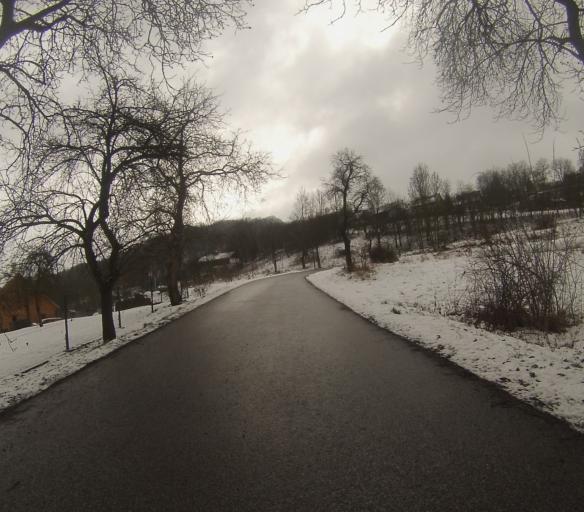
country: CZ
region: Ustecky
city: Benesov nad Ploucnici
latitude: 50.7413
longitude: 14.2670
